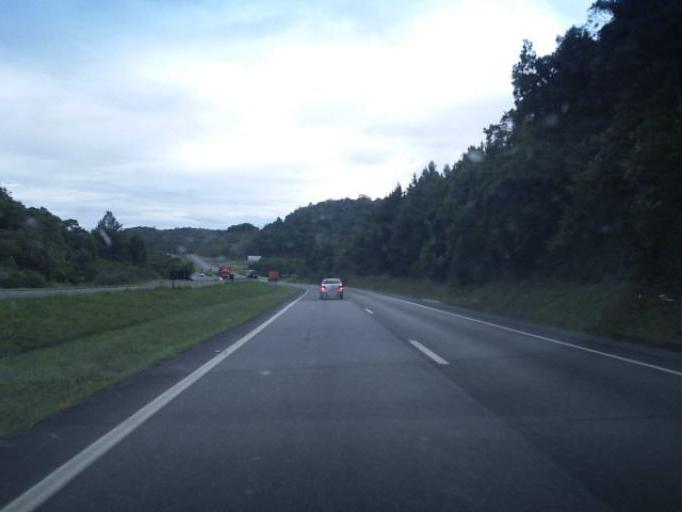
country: BR
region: Parana
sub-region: Campina Grande Do Sul
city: Campina Grande do Sul
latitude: -25.2552
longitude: -48.9125
